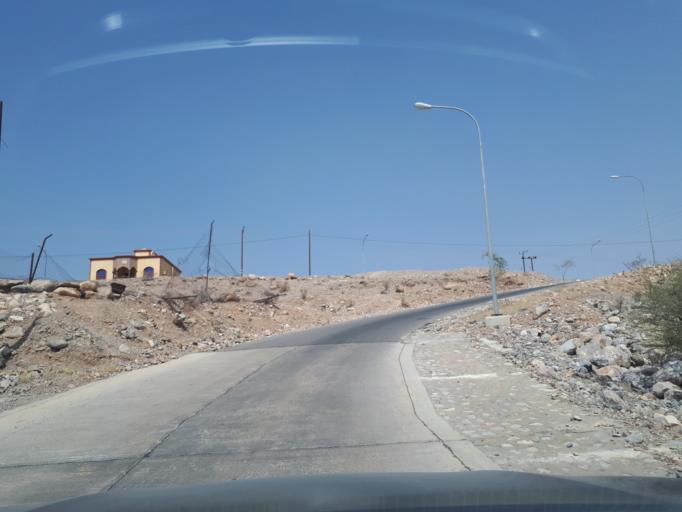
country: OM
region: Ash Sharqiyah
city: Ibra'
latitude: 23.0821
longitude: 58.8668
